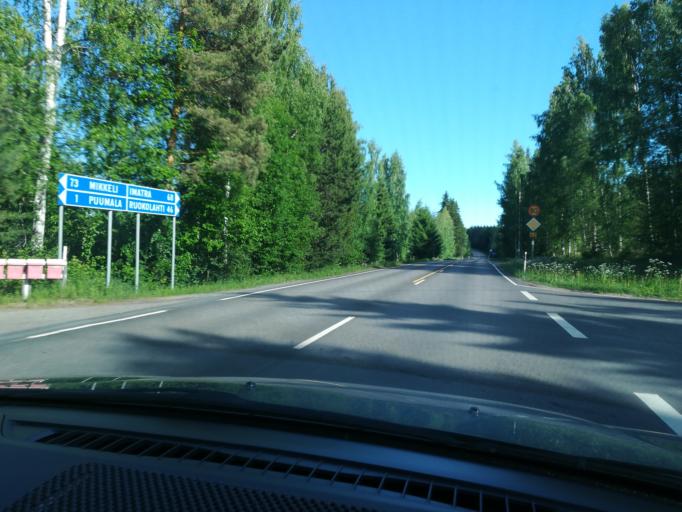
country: FI
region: Southern Savonia
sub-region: Mikkeli
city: Puumala
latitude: 61.5110
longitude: 28.1811
